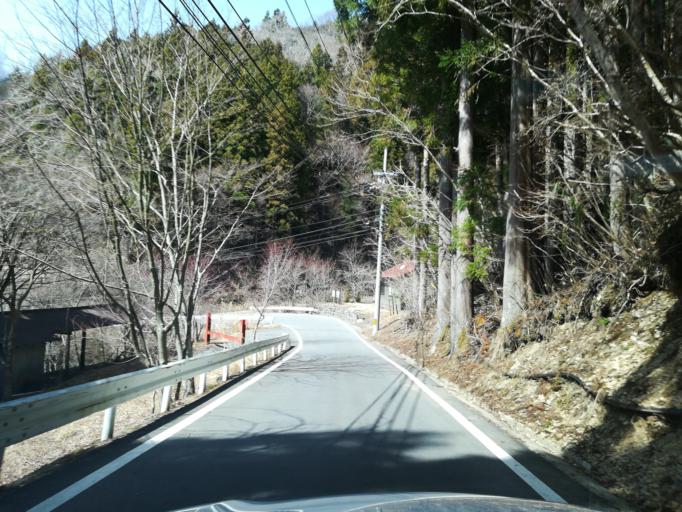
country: JP
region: Tokushima
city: Wakimachi
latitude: 33.8528
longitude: 134.0306
